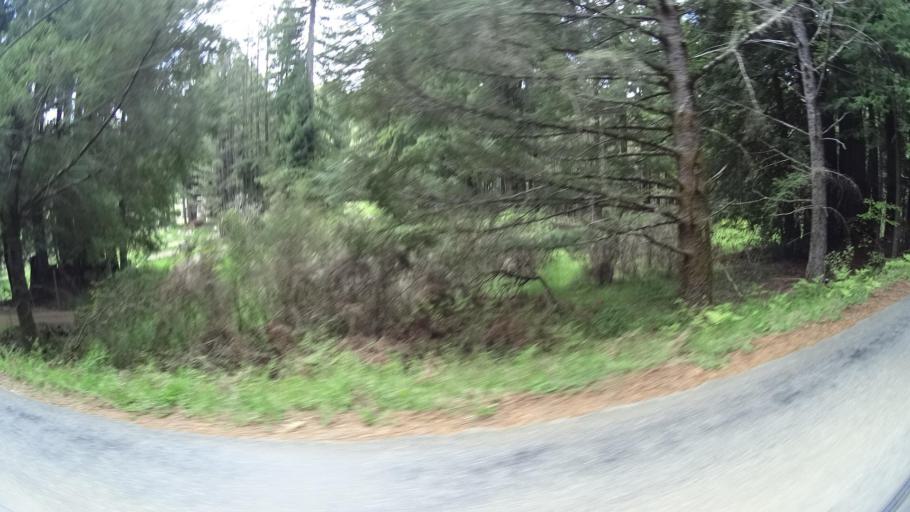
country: US
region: California
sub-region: Humboldt County
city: Redway
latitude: 40.0244
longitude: -123.9443
